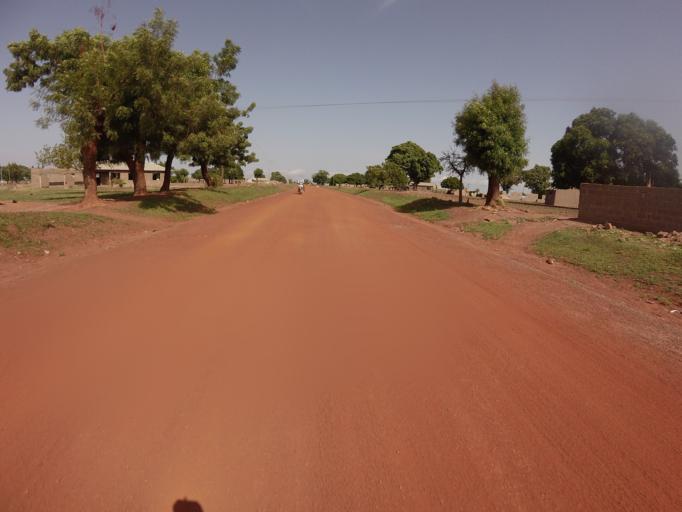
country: GH
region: Upper East
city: Bawku
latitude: 10.8355
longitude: -0.1753
